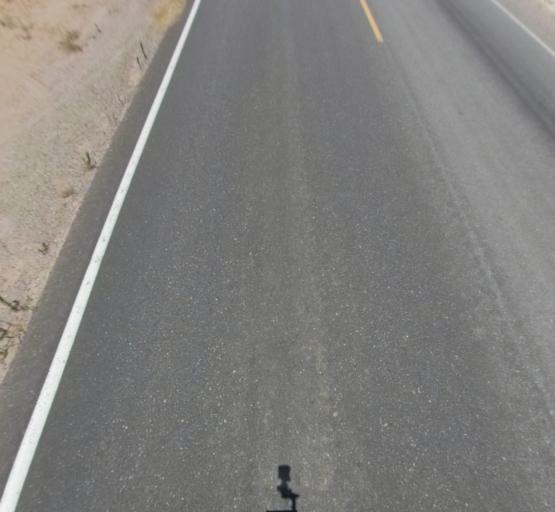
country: US
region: California
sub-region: Madera County
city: Madera
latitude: 36.9329
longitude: -120.0922
